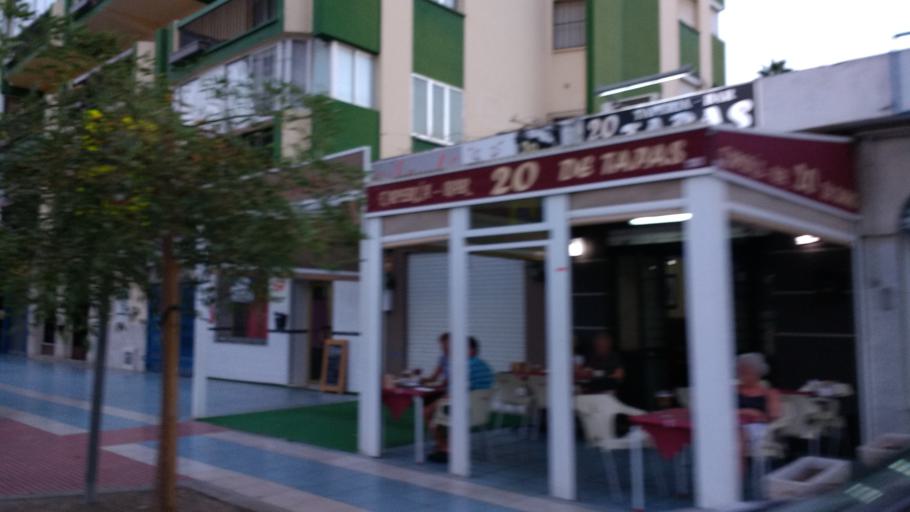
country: ES
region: Andalusia
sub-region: Provincia de Malaga
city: Velez-Malaga
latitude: 36.7381
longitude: -4.0991
